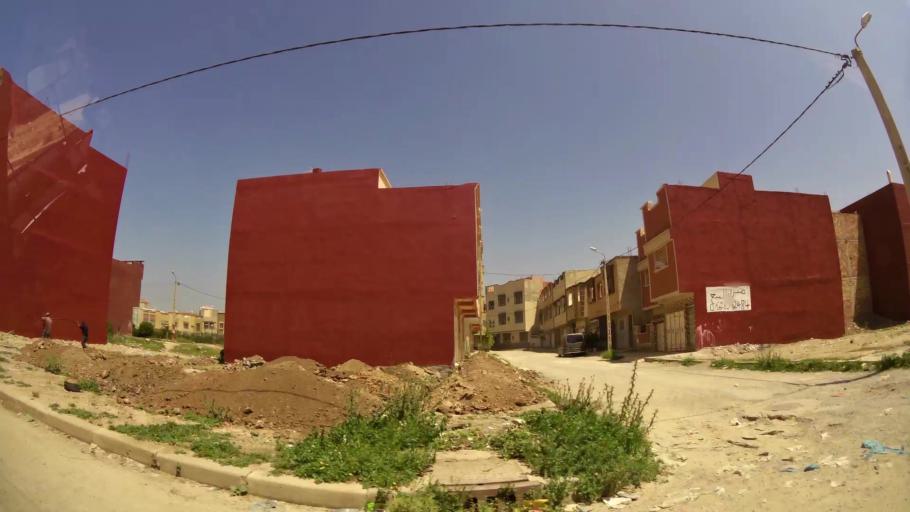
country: MA
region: Oriental
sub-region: Oujda-Angad
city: Oujda
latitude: 34.6978
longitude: -1.8868
